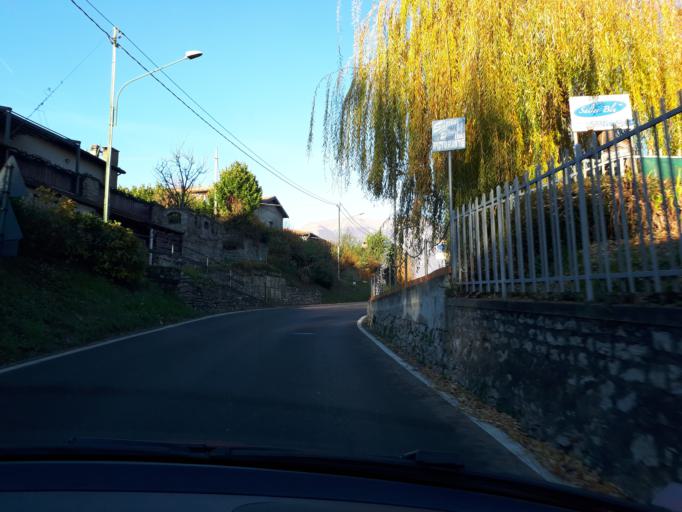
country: IT
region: Lombardy
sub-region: Provincia di Como
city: Bellagio
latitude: 45.9716
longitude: 9.2644
